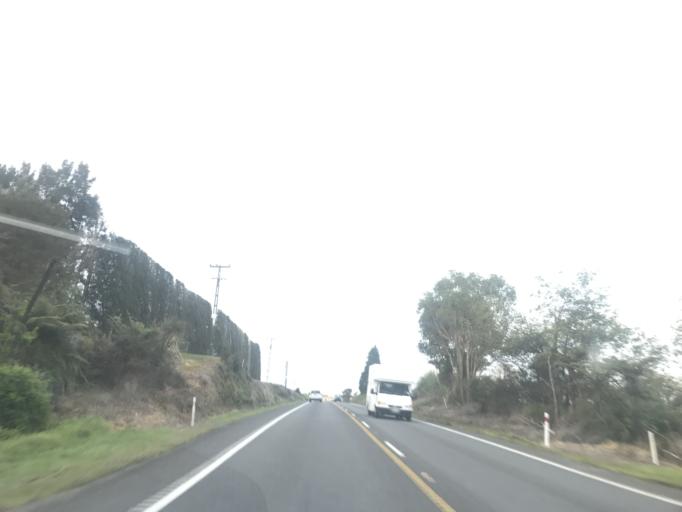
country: NZ
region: Bay of Plenty
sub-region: Western Bay of Plenty District
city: Katikati
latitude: -37.4791
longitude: 175.9311
